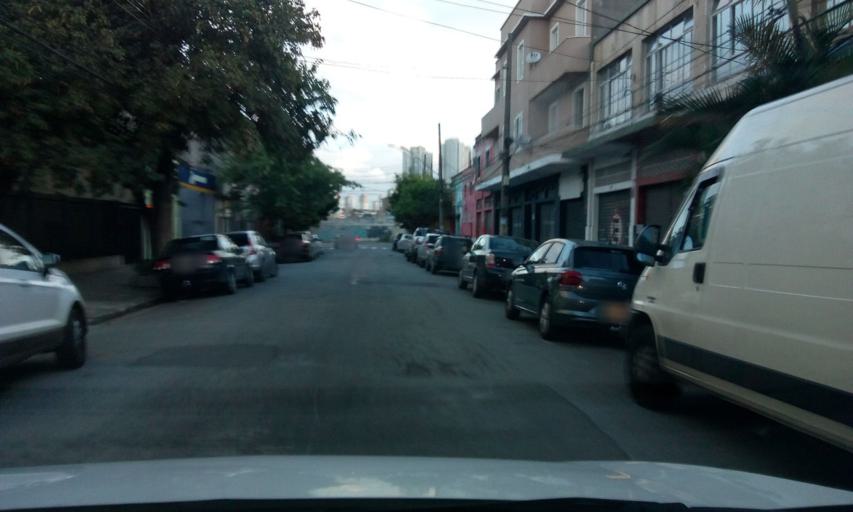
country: BR
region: Sao Paulo
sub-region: Sao Paulo
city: Sao Paulo
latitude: -23.5425
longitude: -46.5934
